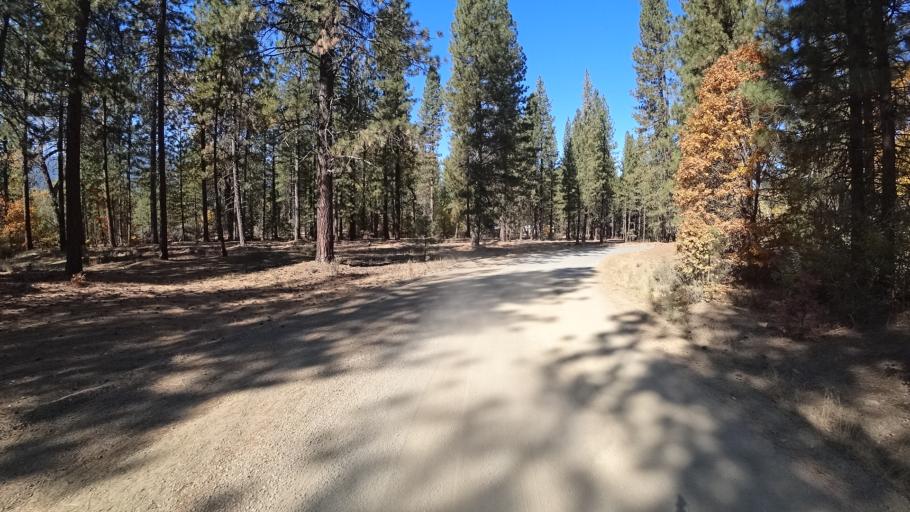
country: US
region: California
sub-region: Siskiyou County
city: Yreka
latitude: 41.5921
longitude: -122.9607
